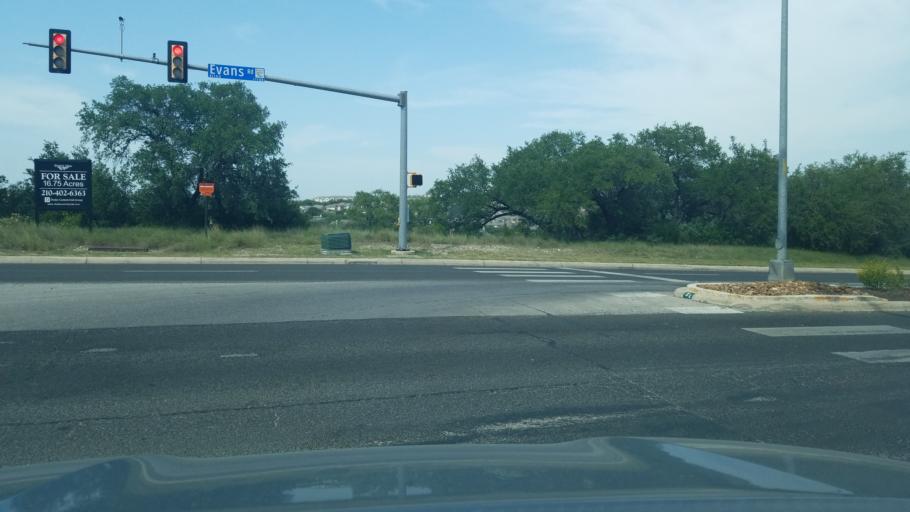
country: US
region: Texas
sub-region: Bexar County
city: Hollywood Park
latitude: 29.6394
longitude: -98.4794
